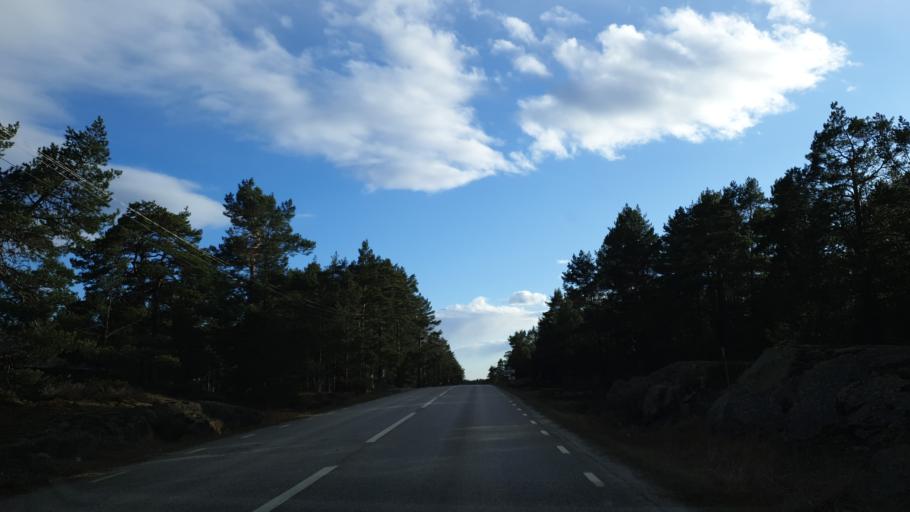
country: SE
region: Stockholm
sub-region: Varmdo Kommun
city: Holo
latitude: 59.3002
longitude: 18.6728
